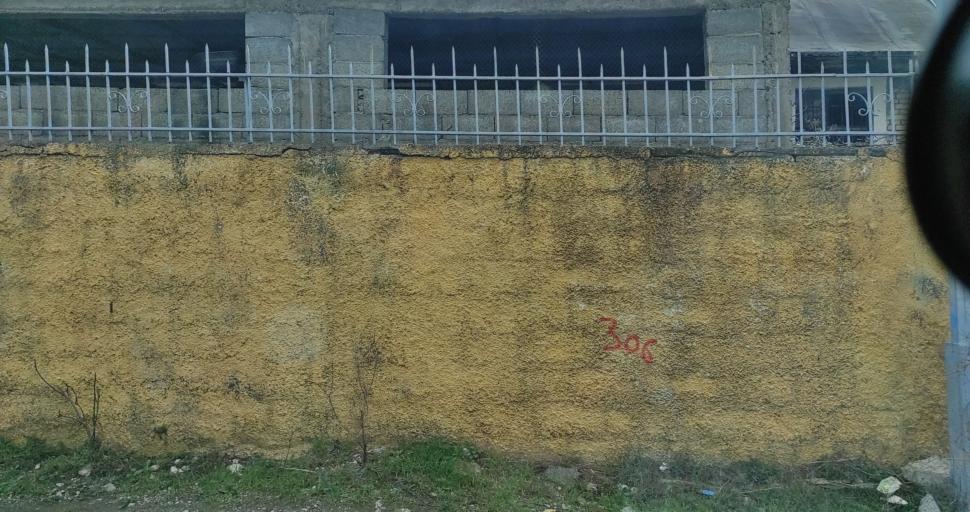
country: AL
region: Lezhe
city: Shengjin
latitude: 41.8151
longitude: 19.5873
